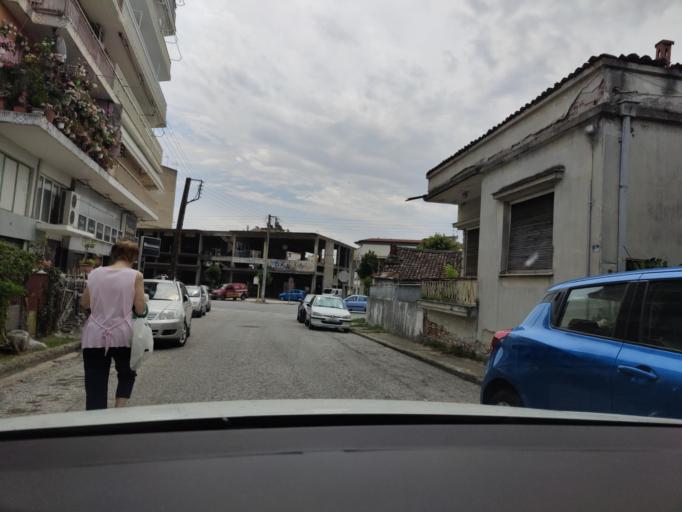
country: GR
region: Central Macedonia
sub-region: Nomos Serron
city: Serres
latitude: 41.0870
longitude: 23.5329
